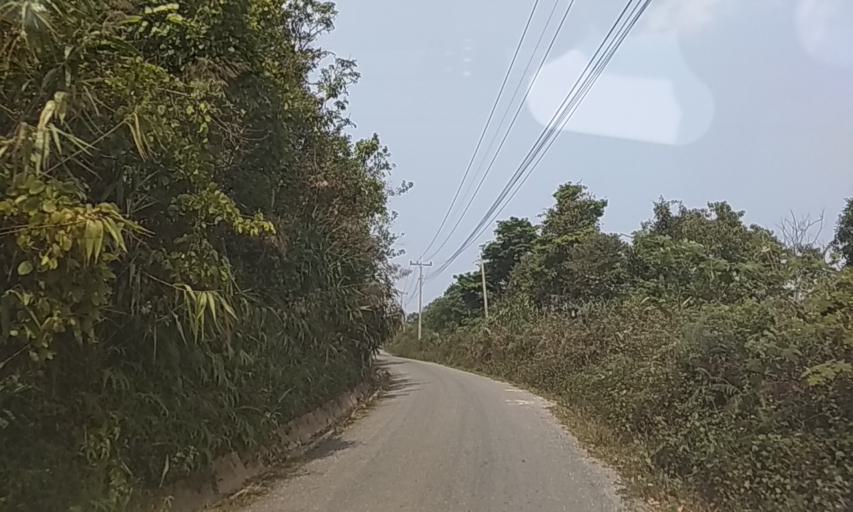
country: TH
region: Nan
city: Chaloem Phra Kiat
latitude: 20.0261
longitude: 101.0965
